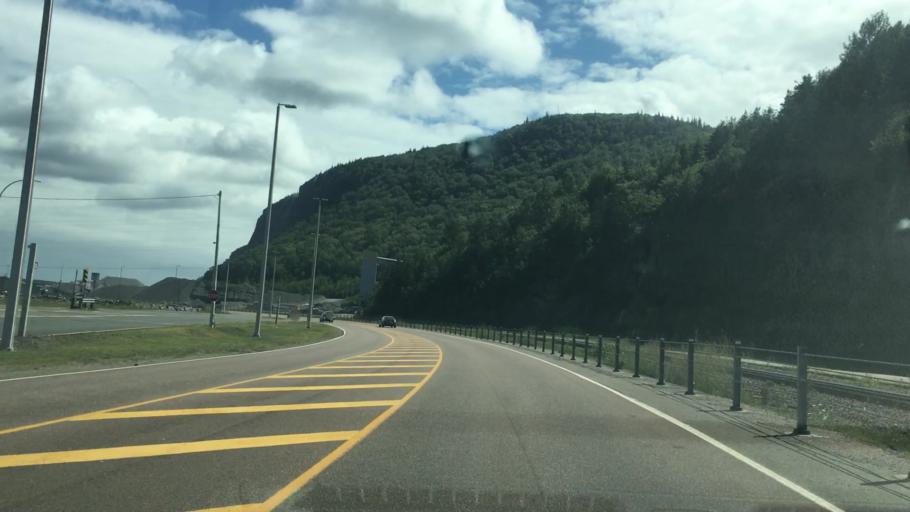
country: CA
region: Nova Scotia
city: Port Hawkesbury
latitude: 45.6421
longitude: -61.4297
